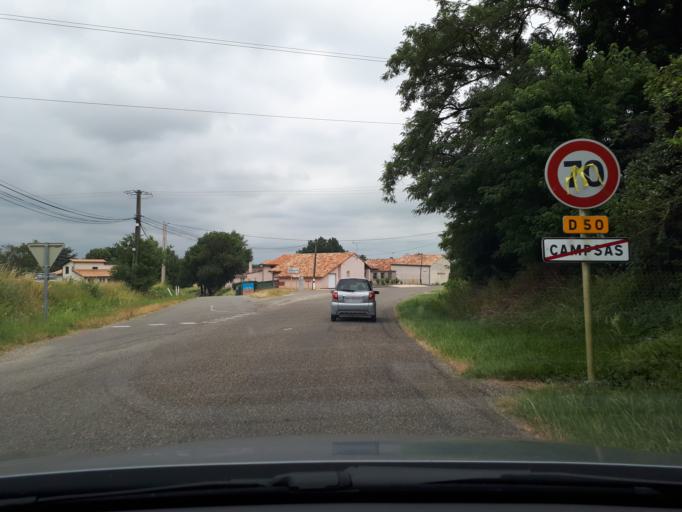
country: FR
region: Midi-Pyrenees
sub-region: Departement du Tarn-et-Garonne
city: Campsas
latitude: 43.8932
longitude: 1.3317
